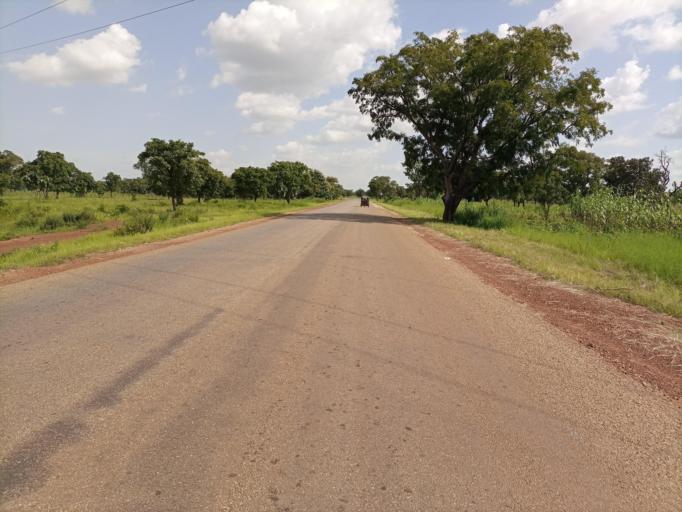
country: GH
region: Northern
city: Savelugu
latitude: 9.5685
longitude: -0.9888
